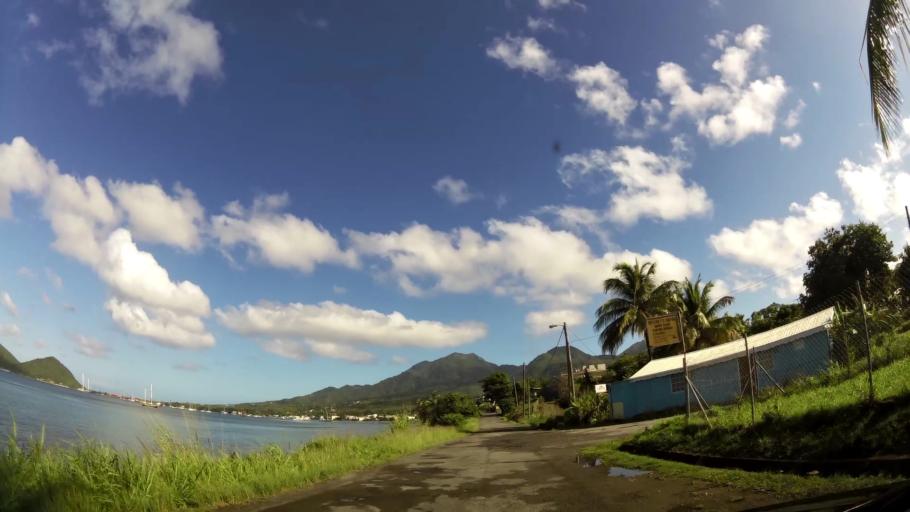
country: DM
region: Saint John
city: Portsmouth
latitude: 15.5646
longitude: -61.4586
